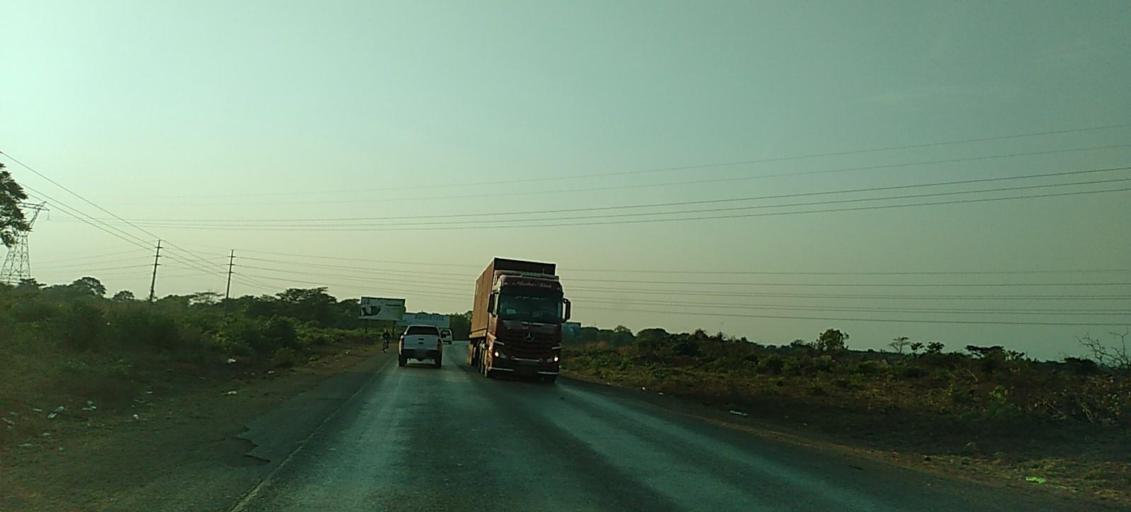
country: ZM
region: Copperbelt
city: Ndola
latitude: -13.0439
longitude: 28.6967
